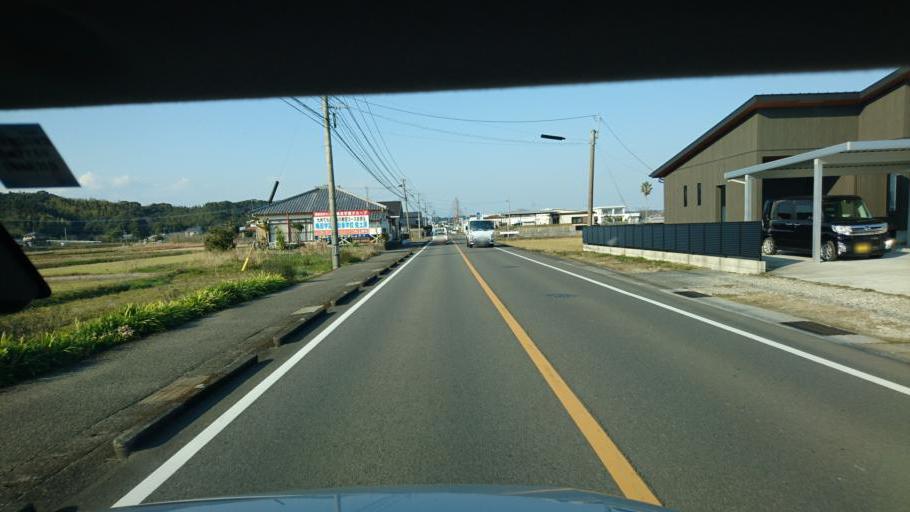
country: JP
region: Miyazaki
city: Miyazaki-shi
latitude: 31.9921
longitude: 131.4395
